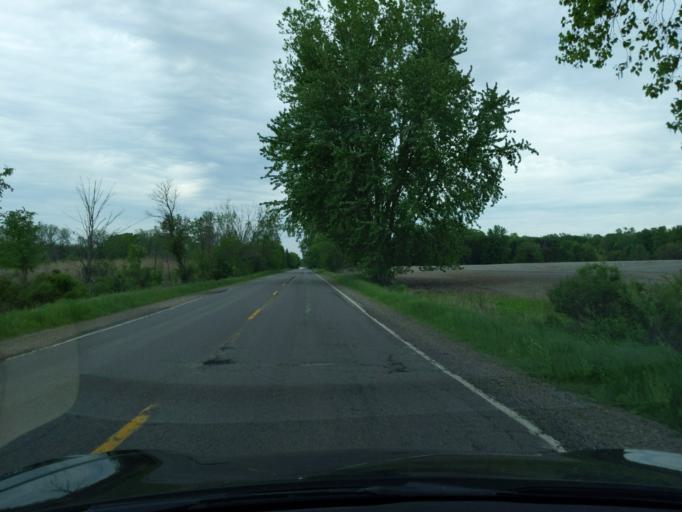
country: US
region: Michigan
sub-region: Ingham County
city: Mason
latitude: 42.6057
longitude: -84.3580
